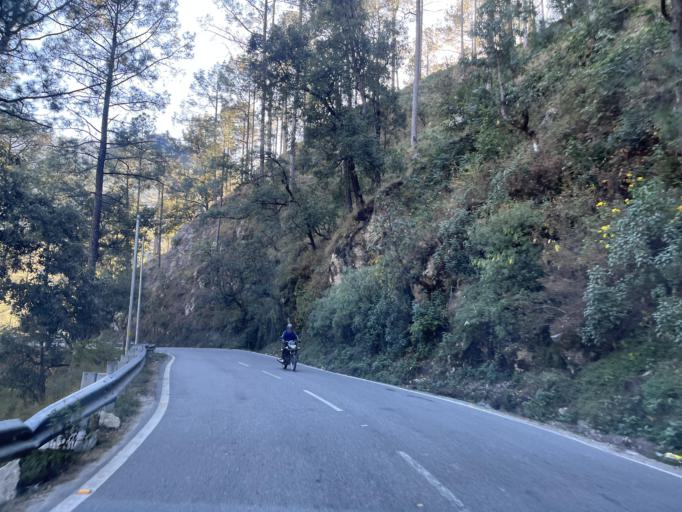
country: IN
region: Uttarakhand
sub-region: Naini Tal
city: Bhowali
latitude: 29.4050
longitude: 79.5108
